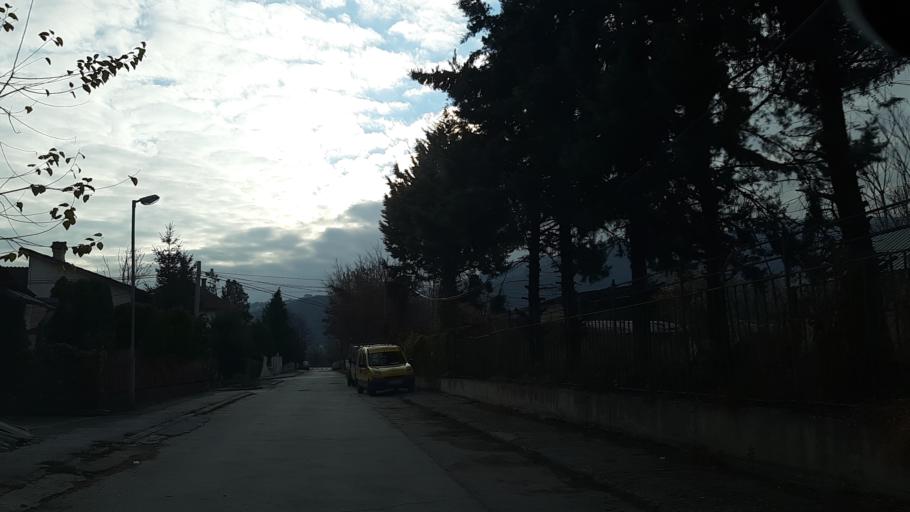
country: MK
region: Kisela Voda
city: Usje
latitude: 41.9782
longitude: 21.4515
